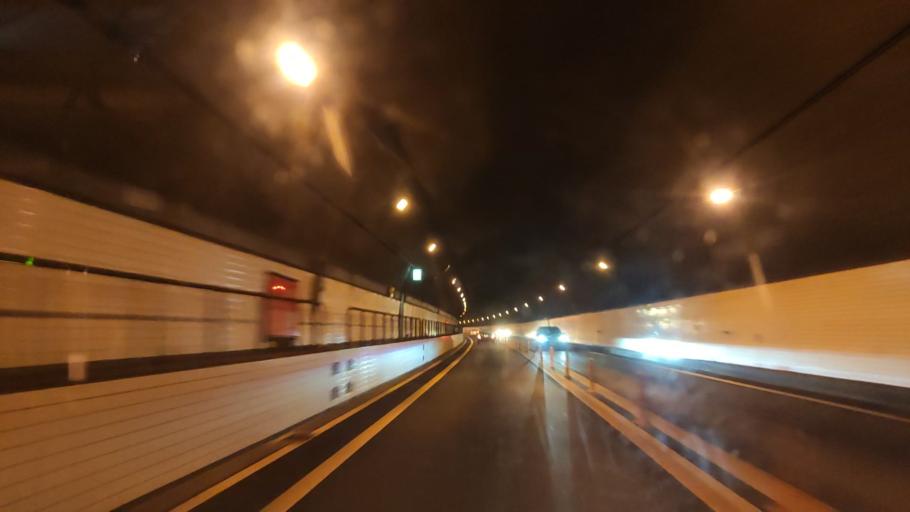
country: JP
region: Tokushima
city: Ikedacho
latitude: 34.0254
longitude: 133.7775
